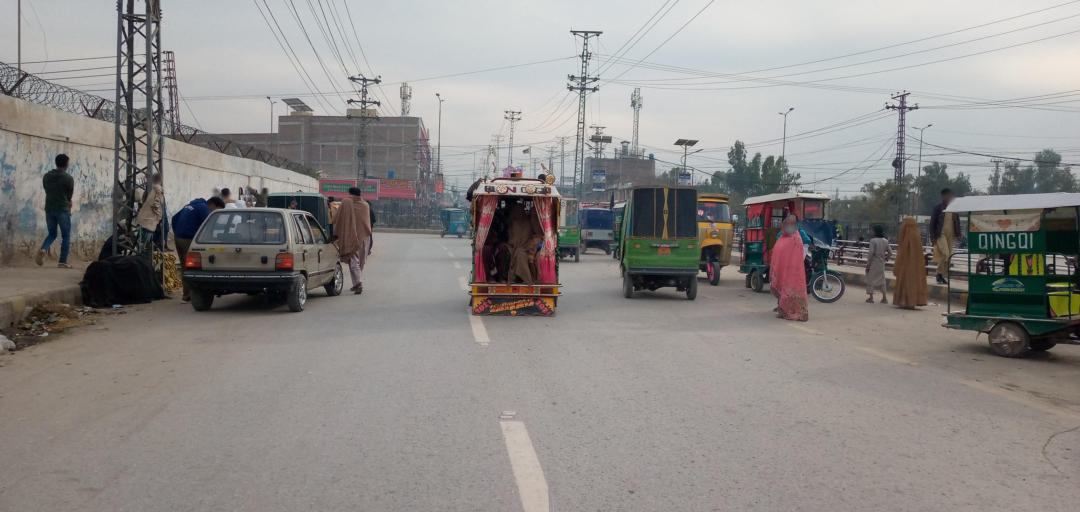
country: PK
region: Khyber Pakhtunkhwa
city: Peshawar
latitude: 33.9987
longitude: 71.4694
